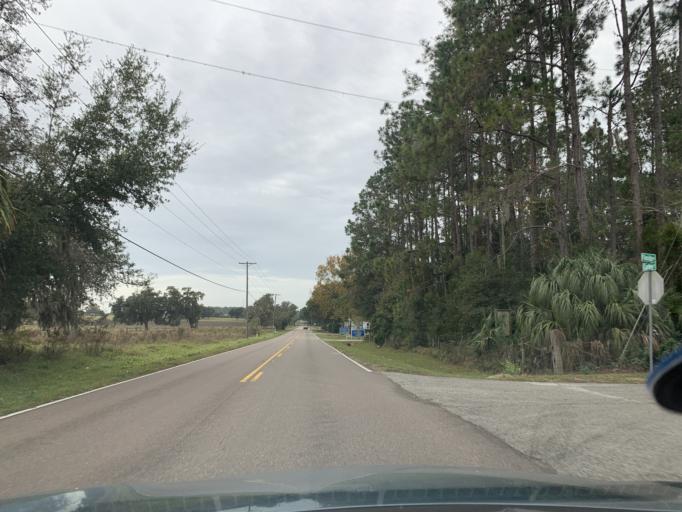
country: US
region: Florida
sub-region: Pasco County
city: San Antonio
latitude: 28.3284
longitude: -82.2743
